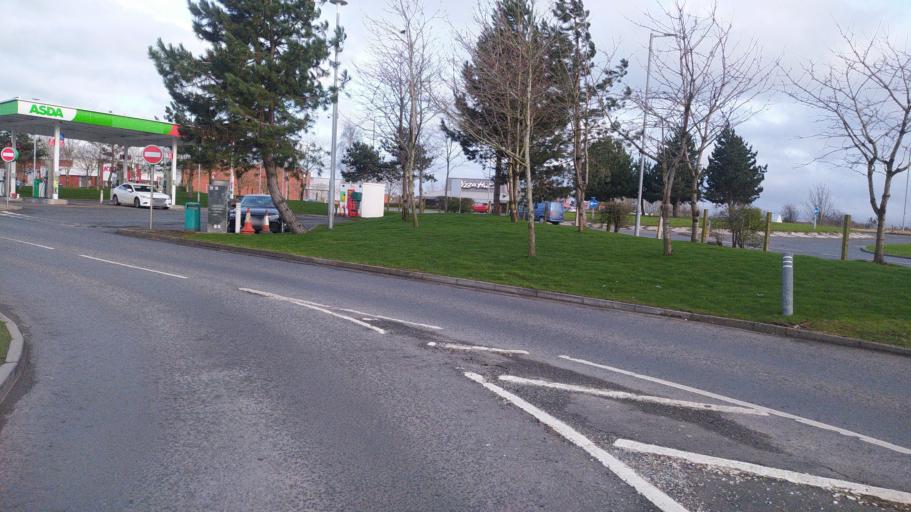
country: GB
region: Scotland
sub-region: South Ayrshire
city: Prestwick
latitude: 55.4786
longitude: -4.5979
